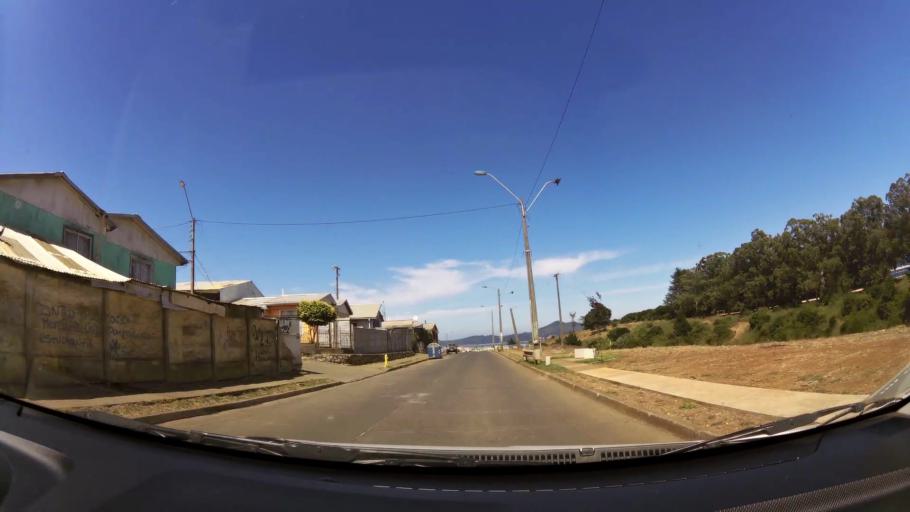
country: CL
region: Biobio
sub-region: Provincia de Concepcion
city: Talcahuano
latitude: -36.7138
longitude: -73.1404
